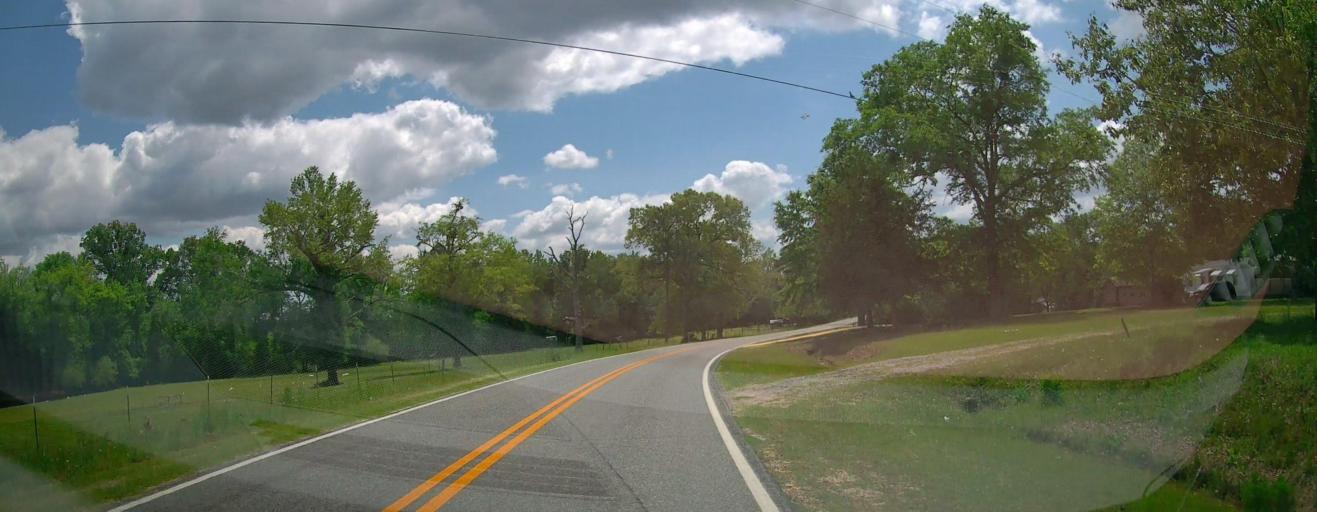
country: US
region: Georgia
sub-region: Laurens County
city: East Dublin
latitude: 32.5549
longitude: -82.8166
